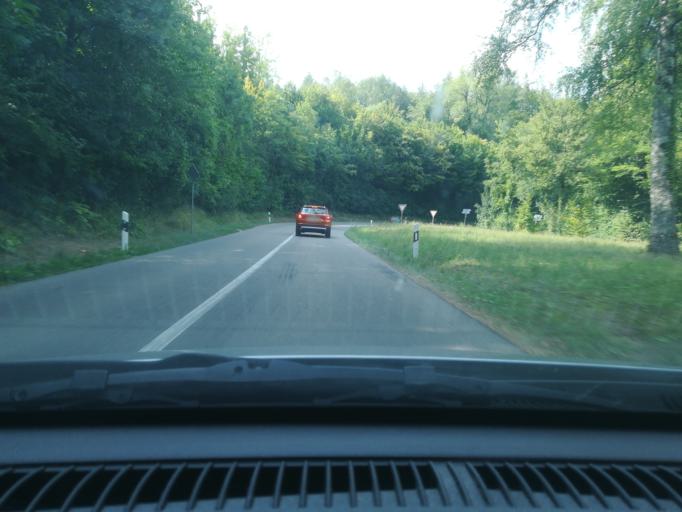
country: CH
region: Schaffhausen
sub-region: Bezirk Reiat
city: Thayngen
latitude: 47.7457
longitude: 8.6923
